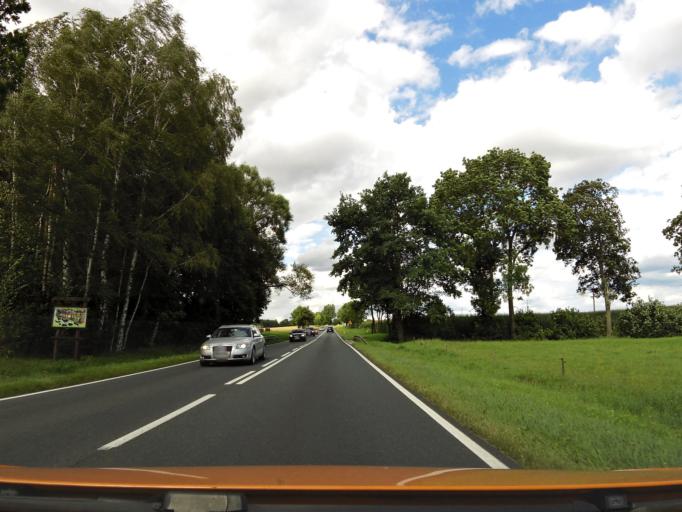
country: PL
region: West Pomeranian Voivodeship
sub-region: Powiat gryficki
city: Ploty
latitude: 53.7371
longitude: 15.2075
